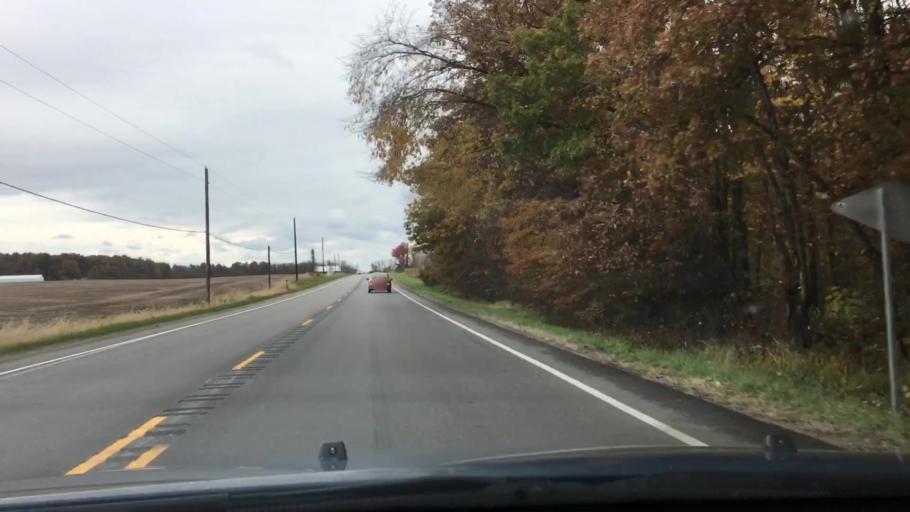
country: US
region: Indiana
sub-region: Adams County
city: Geneva
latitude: 40.5256
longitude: -84.9694
